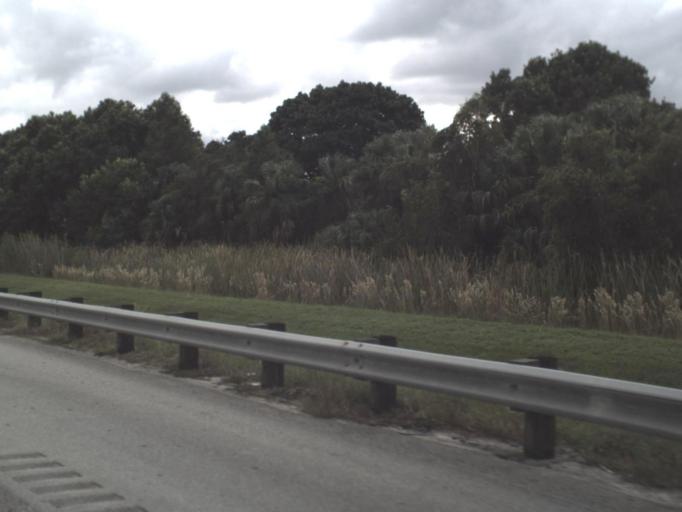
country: US
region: Florida
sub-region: Palm Beach County
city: Palm Beach Gardens
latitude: 26.8214
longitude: -80.1308
